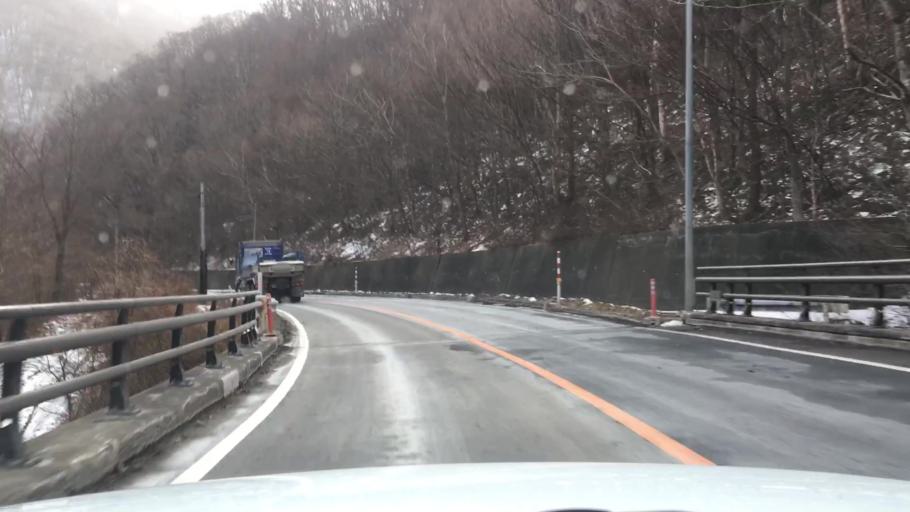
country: JP
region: Iwate
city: Tono
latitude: 39.6208
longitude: 141.5043
